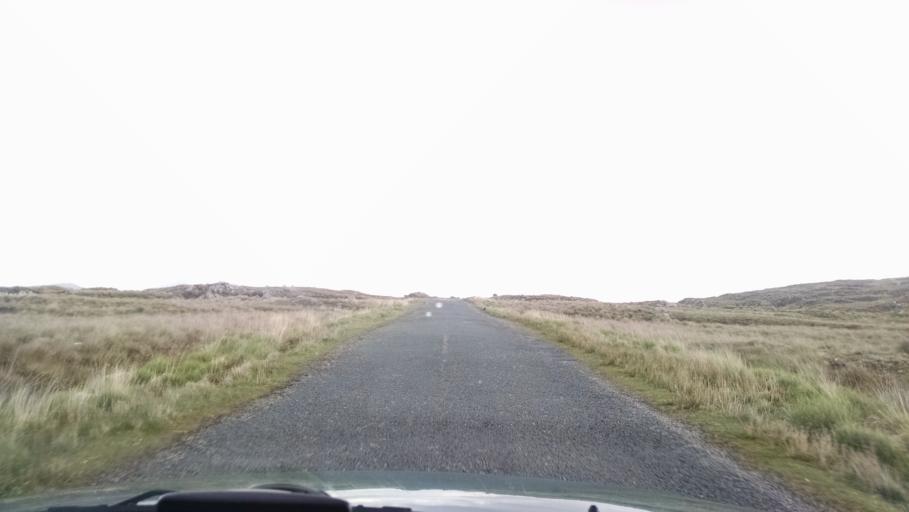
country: IE
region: Connaught
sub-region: County Galway
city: Clifden
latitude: 53.4437
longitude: -9.9282
